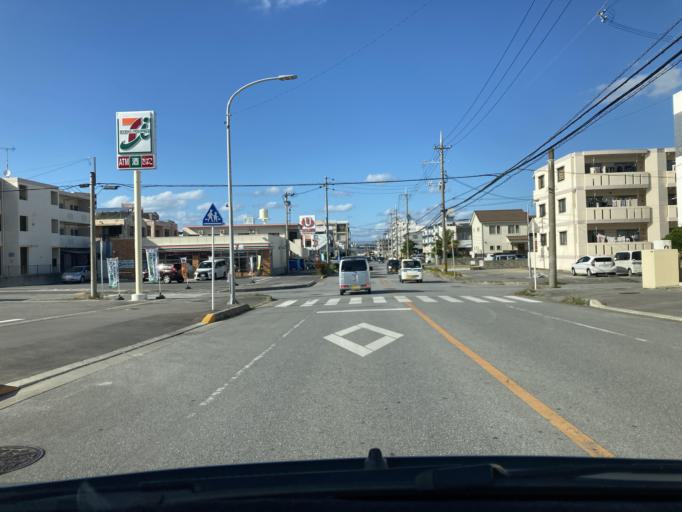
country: JP
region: Okinawa
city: Okinawa
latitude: 26.3407
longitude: 127.8248
